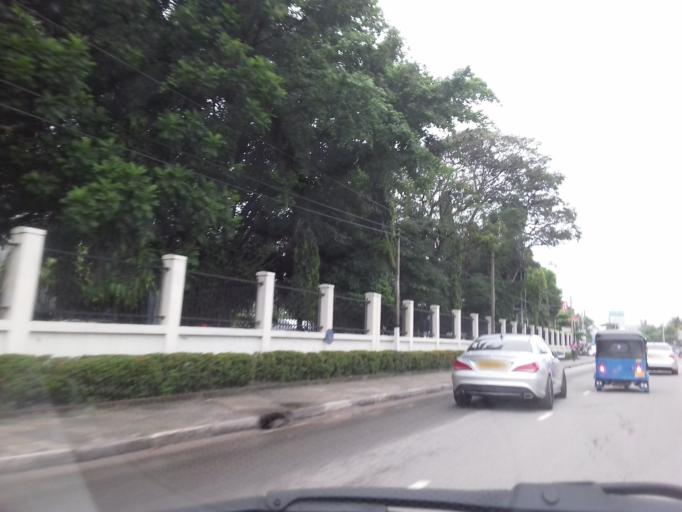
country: LK
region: Western
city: Pita Kotte
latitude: 6.9071
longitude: 79.9008
